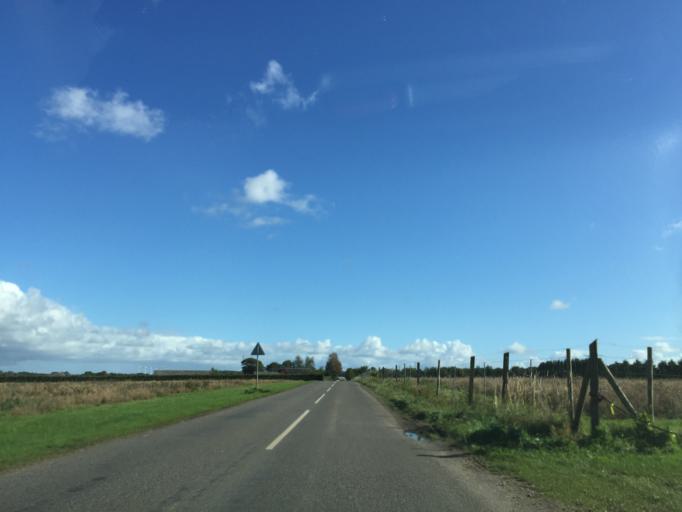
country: DK
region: Central Jutland
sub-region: Viborg Kommune
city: Bjerringbro
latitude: 56.3953
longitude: 9.6507
